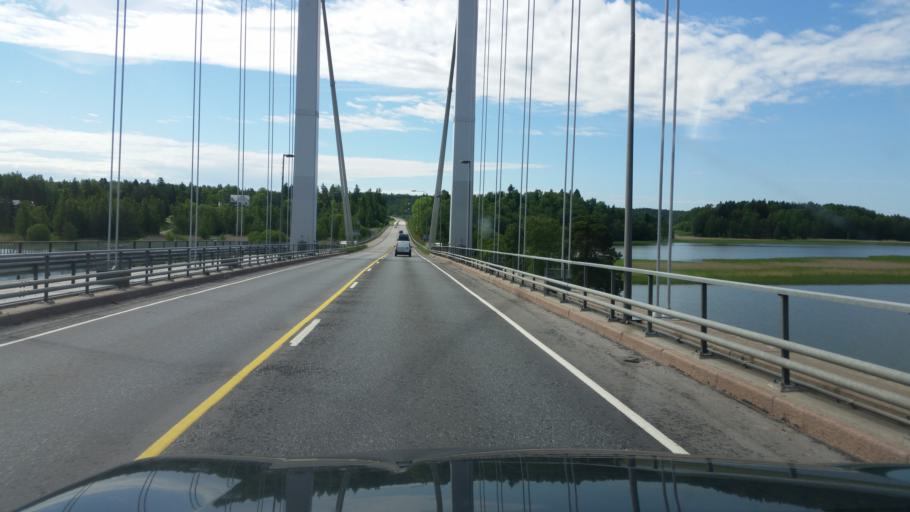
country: FI
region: Varsinais-Suomi
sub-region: Turku
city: Kaarina
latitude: 60.3656
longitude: 22.3583
